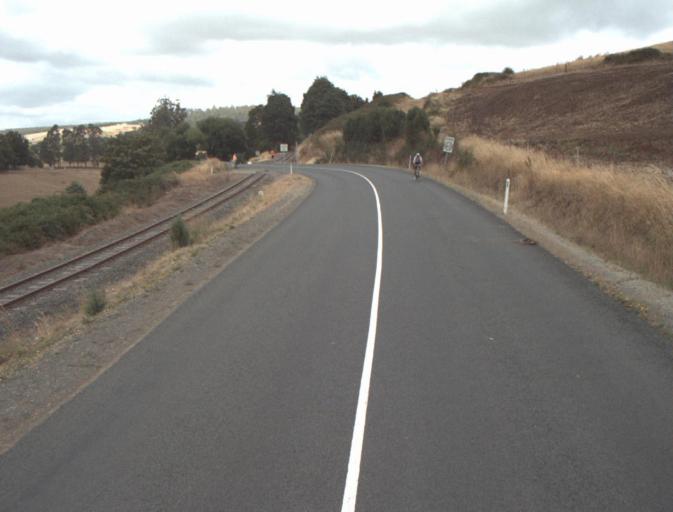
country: AU
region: Tasmania
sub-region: Launceston
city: Mayfield
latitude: -41.1822
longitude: 147.2228
